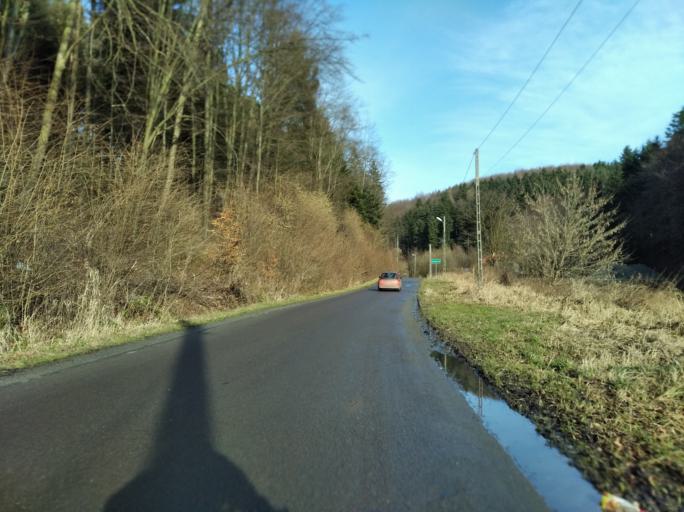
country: PL
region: Subcarpathian Voivodeship
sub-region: Powiat strzyzowski
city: Strzyzow
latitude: 49.8841
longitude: 21.7746
